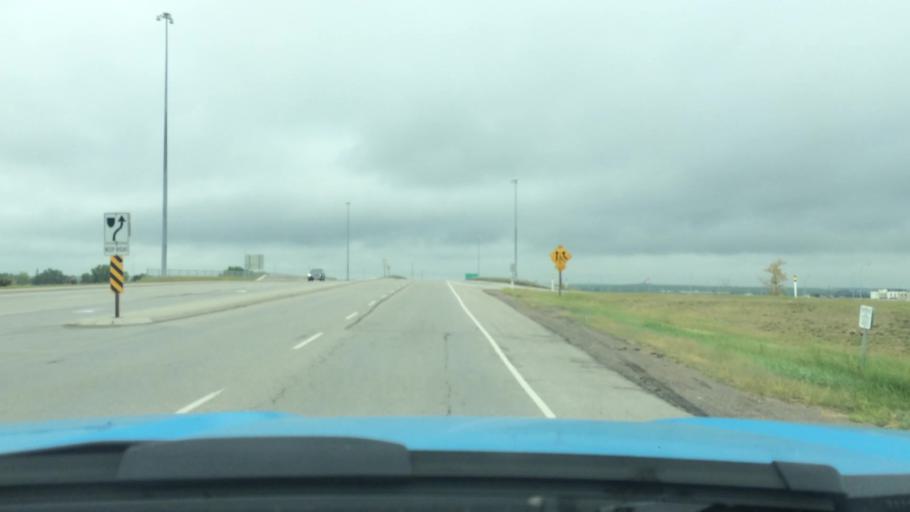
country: CA
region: Alberta
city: Airdrie
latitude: 51.3001
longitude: -113.9987
